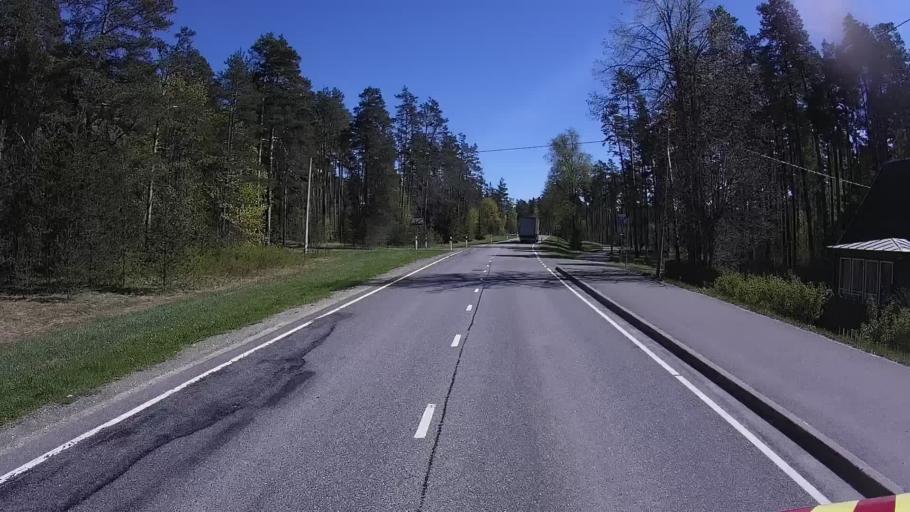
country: EE
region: Harju
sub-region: Kuusalu vald
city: Kuusalu
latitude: 59.2813
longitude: 25.6148
